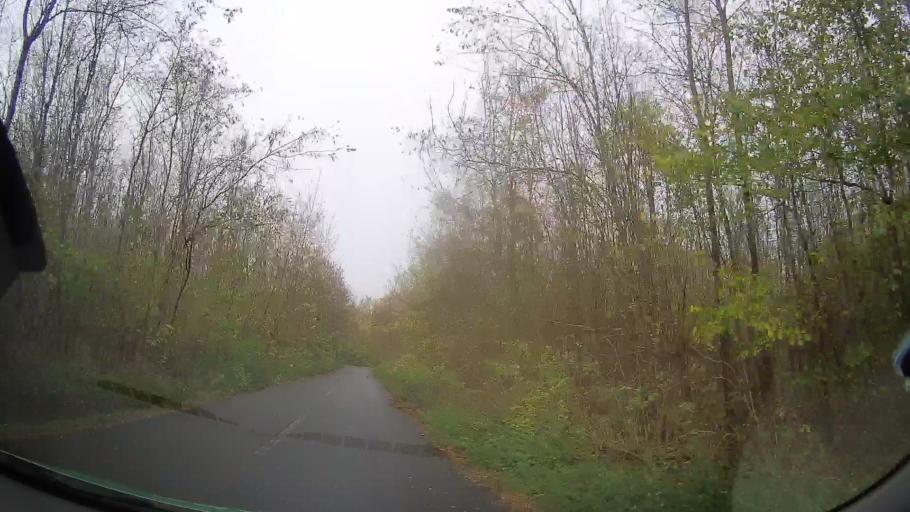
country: RO
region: Prahova
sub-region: Comuna Balta Doamnei
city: Balta Doamnei
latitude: 44.7596
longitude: 26.1311
